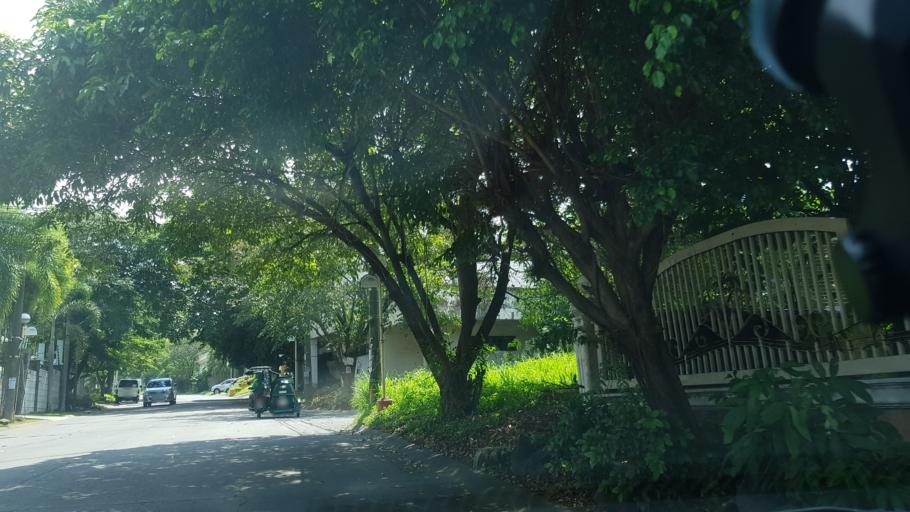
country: PH
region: Calabarzon
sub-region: Province of Rizal
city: Las Pinas
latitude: 14.4268
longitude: 120.9896
